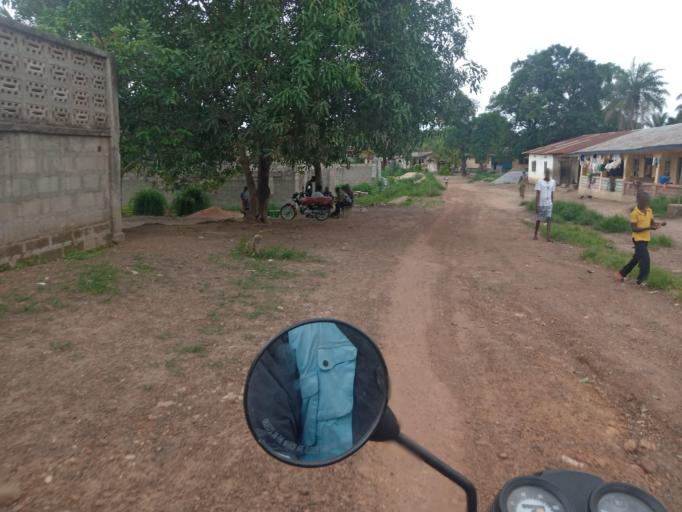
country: SL
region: Southern Province
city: Bo
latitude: 7.9879
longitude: -11.7429
